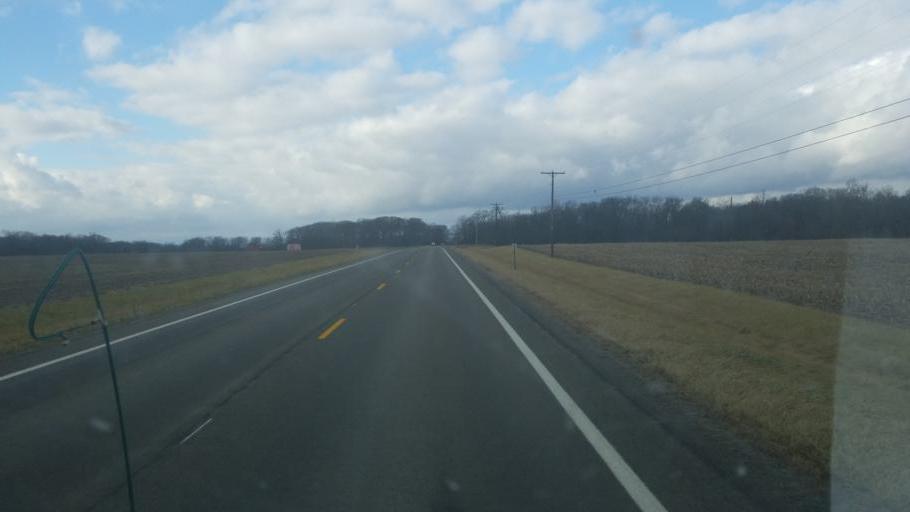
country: US
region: Ohio
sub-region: Wyandot County
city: Upper Sandusky
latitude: 40.7863
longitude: -83.2538
